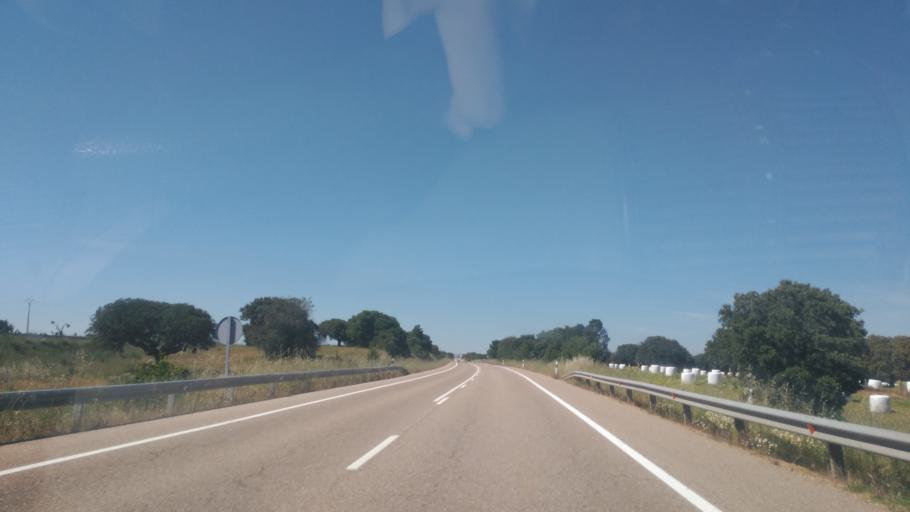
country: ES
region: Castille and Leon
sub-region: Provincia de Salamanca
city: Calzada de Valdunciel
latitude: 41.1452
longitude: -5.6954
